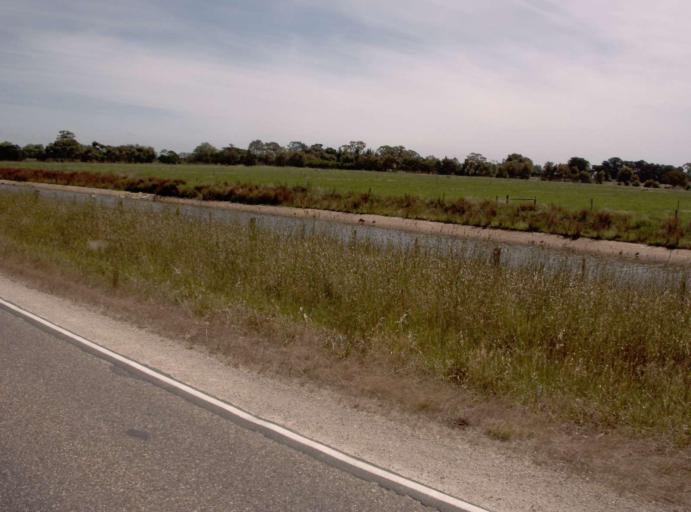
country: AU
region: Victoria
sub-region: Wellington
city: Heyfield
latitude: -38.0498
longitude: 146.8752
